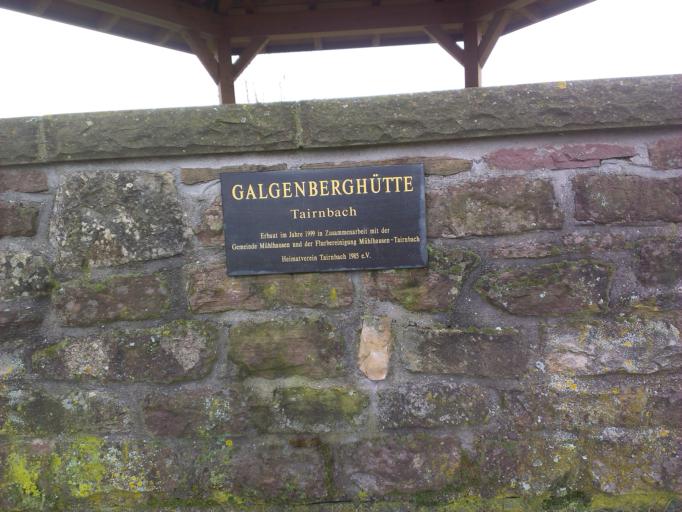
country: DE
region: Baden-Wuerttemberg
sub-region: Karlsruhe Region
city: Balzfeld
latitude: 49.2560
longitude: 8.7618
